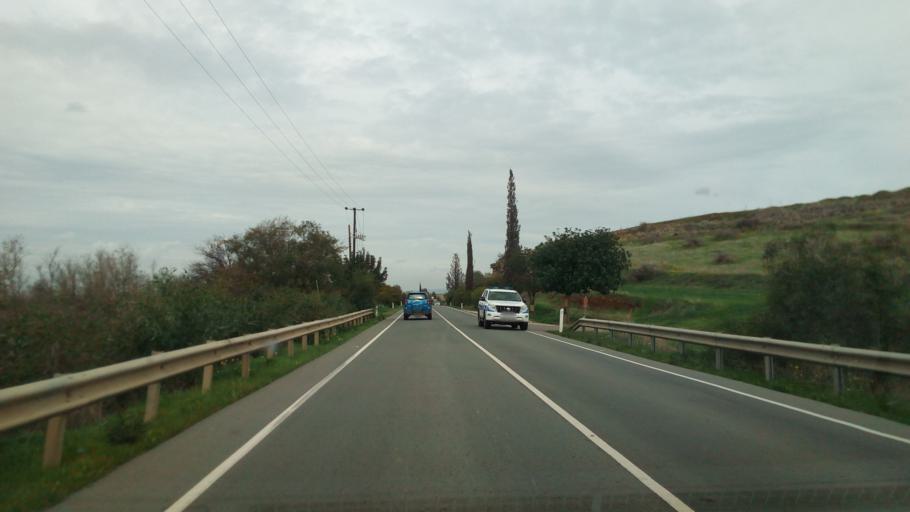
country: CY
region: Lefkosia
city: Astromeritis
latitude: 35.1008
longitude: 32.9708
